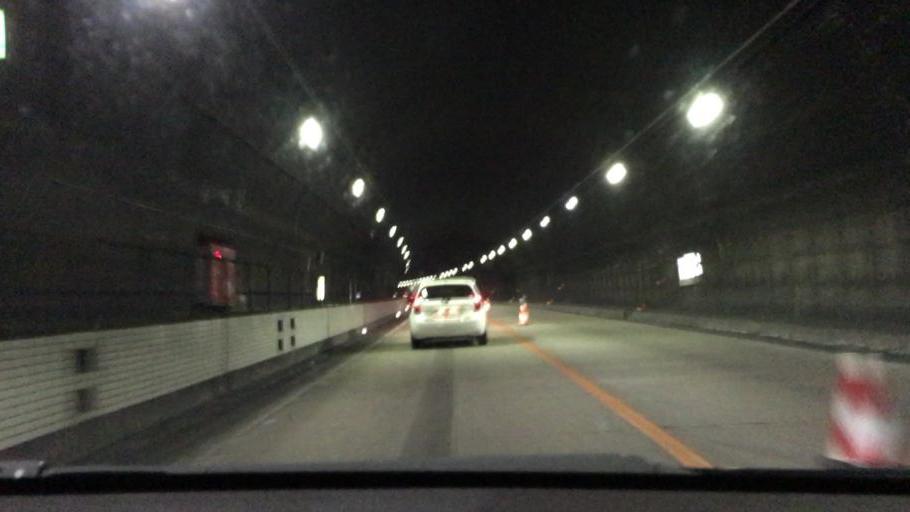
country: JP
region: Yamaguchi
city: Tokuyama
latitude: 34.0912
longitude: 131.7682
